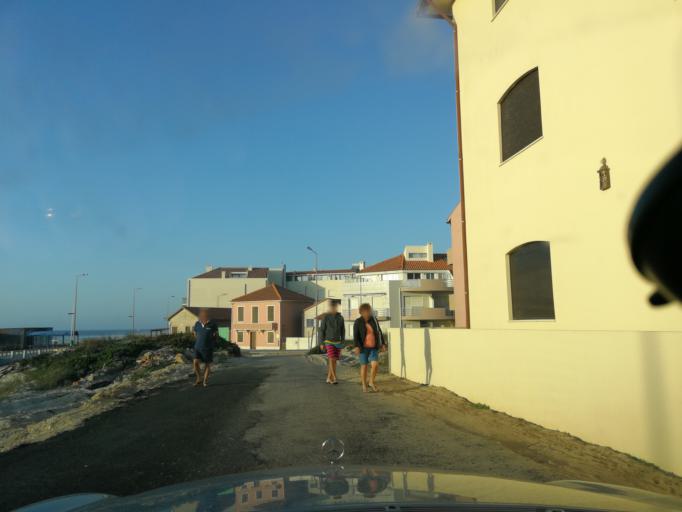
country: PT
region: Aveiro
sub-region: Murtosa
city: Murtosa
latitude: 40.7595
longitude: -8.7133
